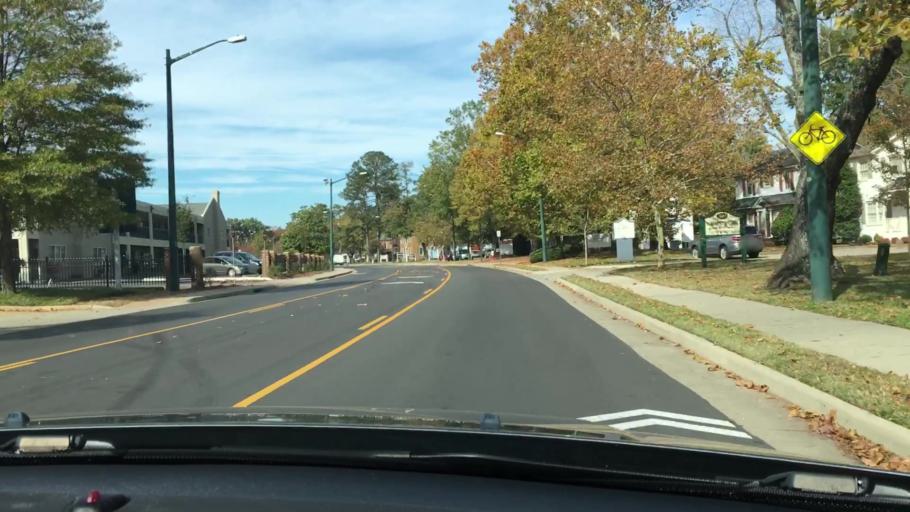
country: US
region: Virginia
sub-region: City of Williamsburg
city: Williamsburg
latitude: 37.2781
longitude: -76.7162
